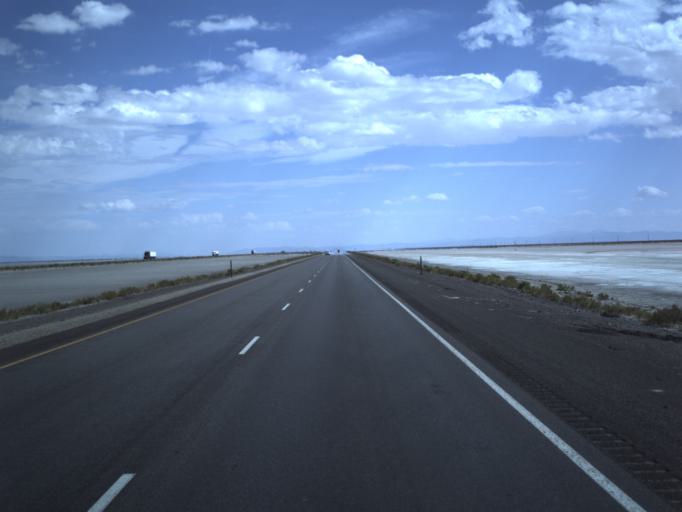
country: US
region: Utah
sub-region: Tooele County
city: Wendover
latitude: 40.7364
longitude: -113.7477
